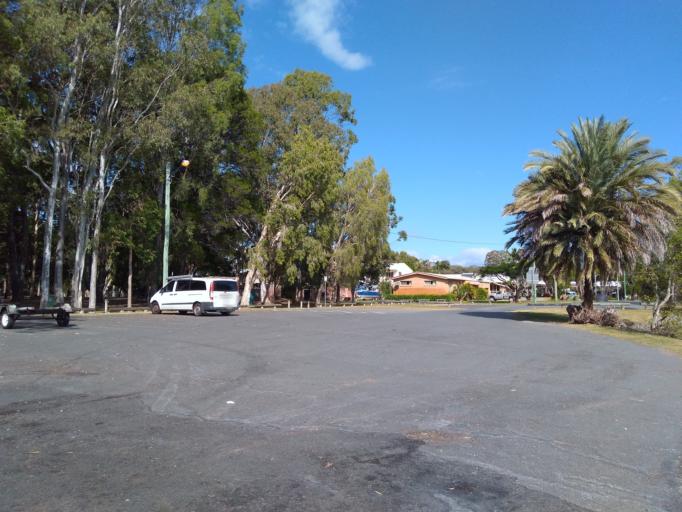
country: AU
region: Queensland
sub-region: Gold Coast
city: Oxenford
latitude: -27.8895
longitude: 153.3834
